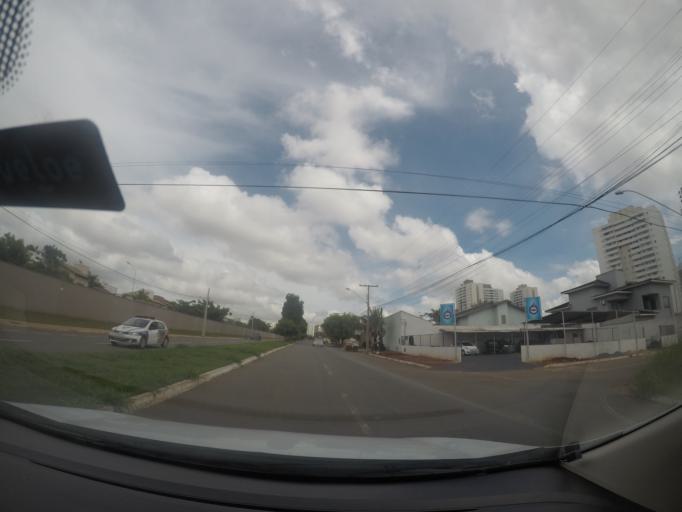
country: BR
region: Goias
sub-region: Goiania
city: Goiania
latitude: -16.7148
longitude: -49.3232
